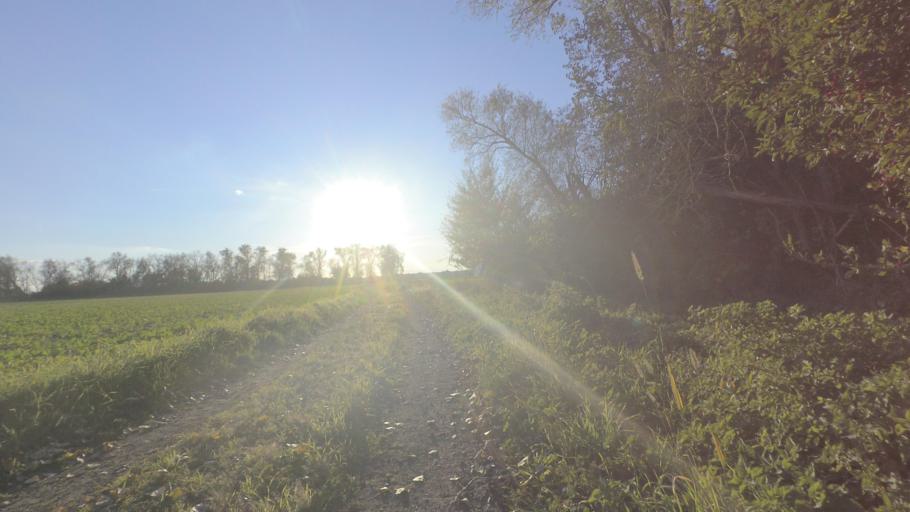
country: DE
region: Brandenburg
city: Ludwigsfelde
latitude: 52.2820
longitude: 13.3302
